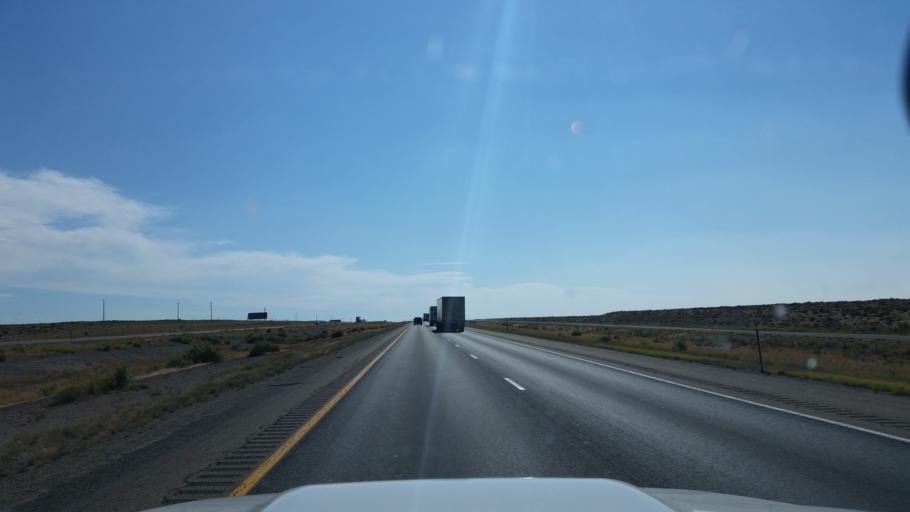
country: US
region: Wyoming
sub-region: Uinta County
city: Lyman
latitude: 41.5284
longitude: -109.9482
